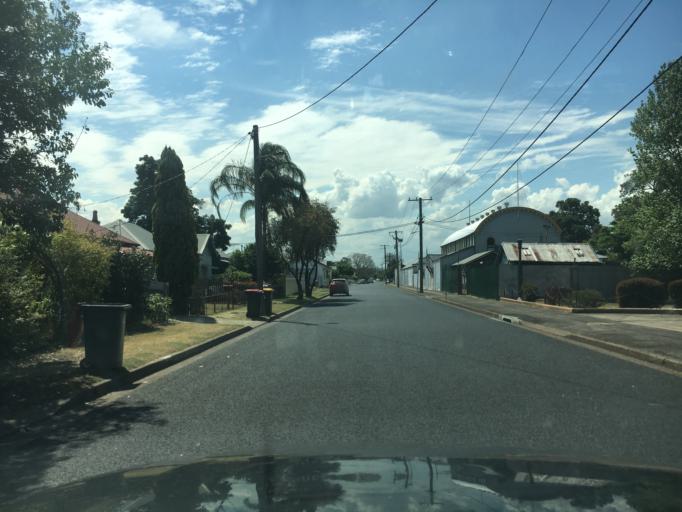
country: AU
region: New South Wales
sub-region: Singleton
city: Singleton
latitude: -32.5702
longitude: 151.1684
